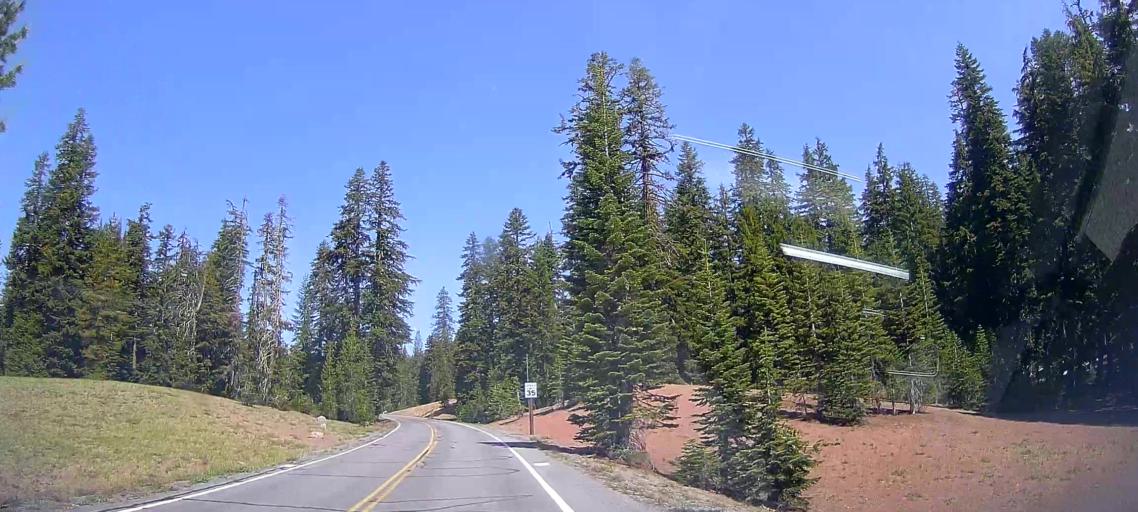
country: US
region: Oregon
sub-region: Klamath County
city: Klamath Falls
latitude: 42.8778
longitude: -122.1081
